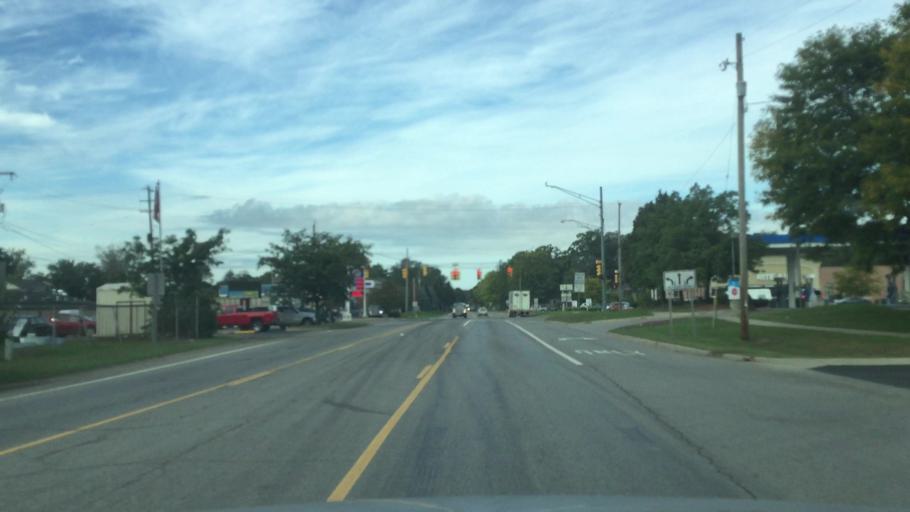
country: US
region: Michigan
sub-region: Oakland County
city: Holly
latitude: 42.8064
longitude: -83.6269
